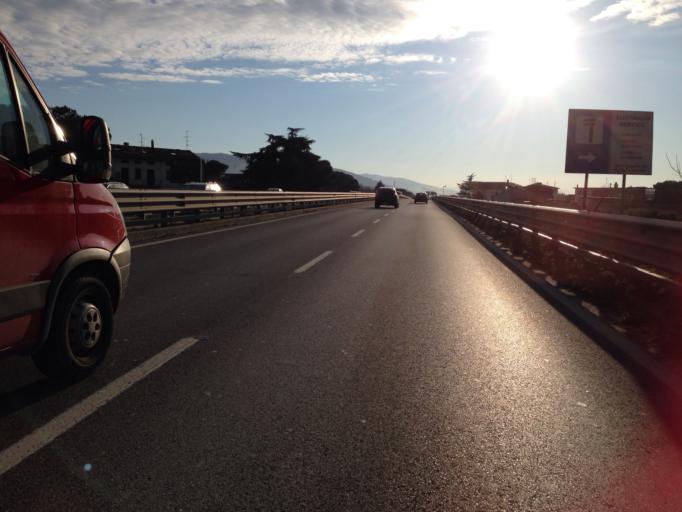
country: IT
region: Tuscany
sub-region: Provincia di Prato
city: Prato
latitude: 43.8810
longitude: 11.0540
